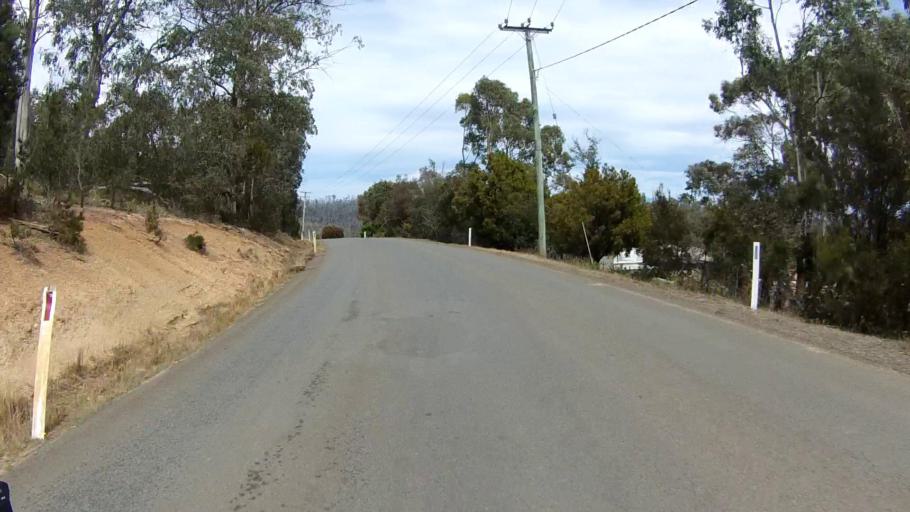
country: AU
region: Tasmania
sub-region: Sorell
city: Sorell
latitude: -42.8006
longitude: 147.6785
